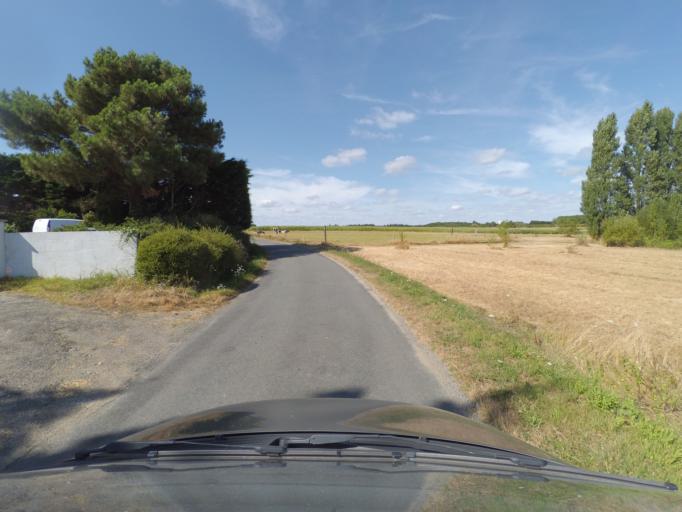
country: FR
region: Pays de la Loire
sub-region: Departement de la Loire-Atlantique
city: Le Bignon
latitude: 47.0873
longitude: -1.4607
